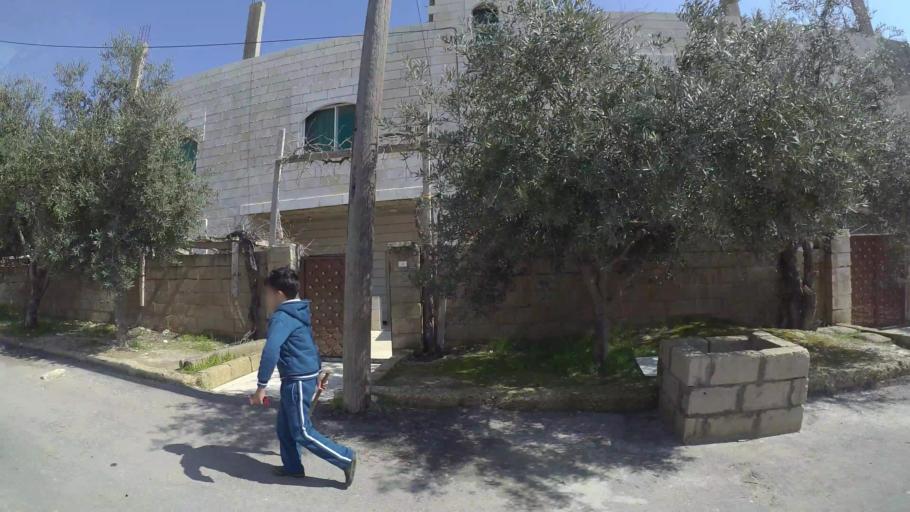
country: JO
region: Amman
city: Al Bunayyat ash Shamaliyah
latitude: 31.8993
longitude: 35.9021
